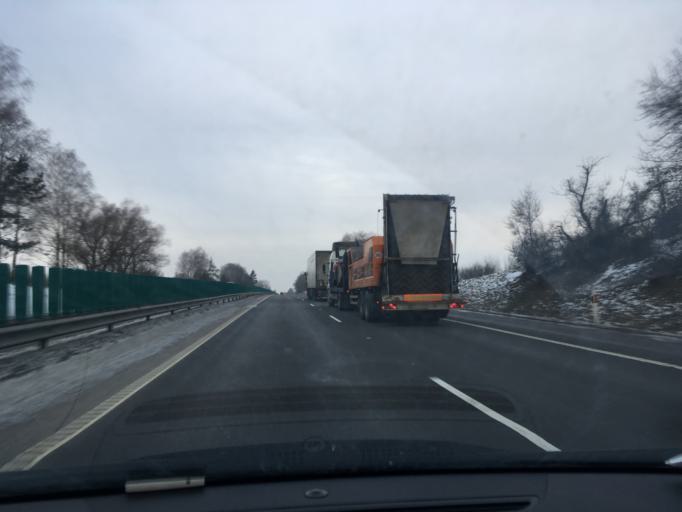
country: LT
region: Vilnius County
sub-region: Vilniaus Rajonas
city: Vievis
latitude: 54.7820
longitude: 24.7605
